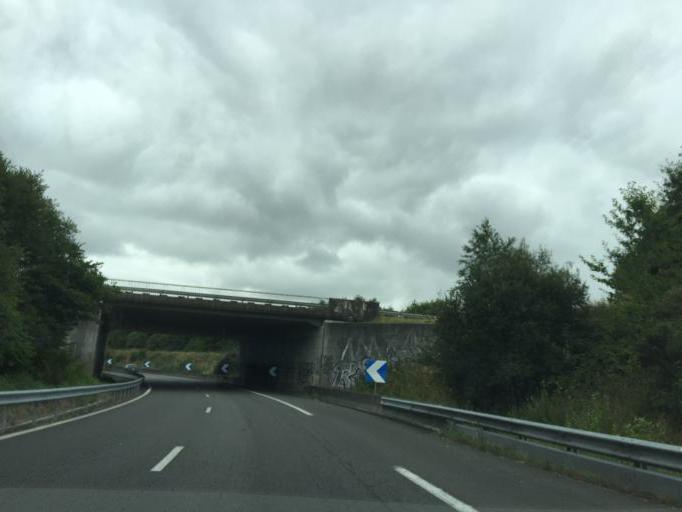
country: FR
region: Brittany
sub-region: Departement d'Ille-et-Vilaine
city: Cesson-Sevigne
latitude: 48.1159
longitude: -1.5730
